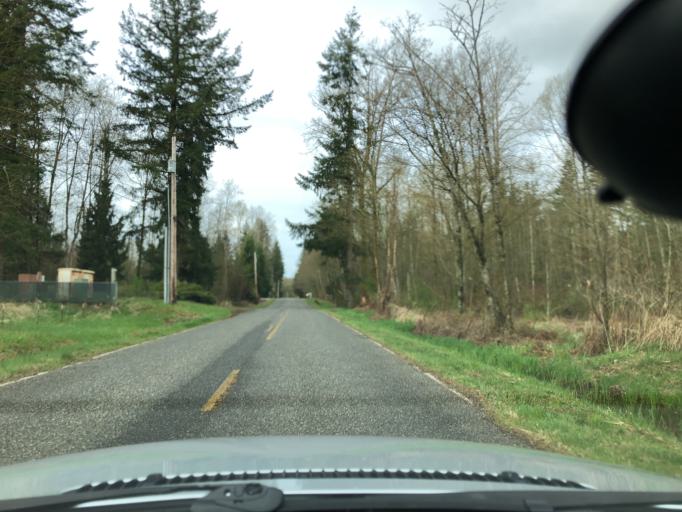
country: CA
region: British Columbia
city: Langley
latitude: 48.9789
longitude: -122.6061
